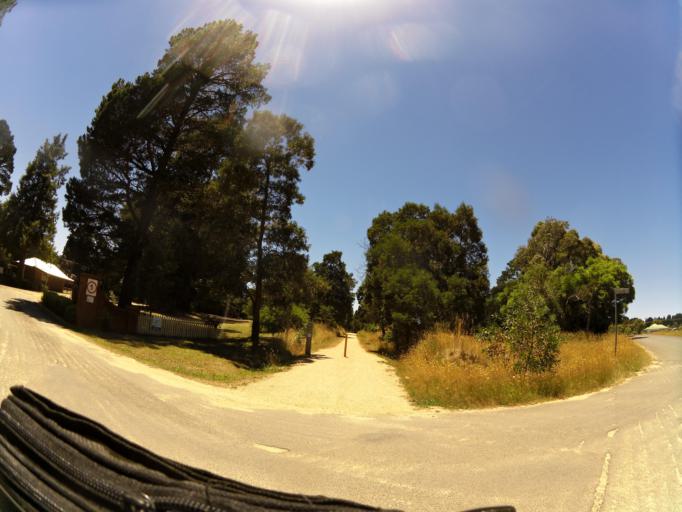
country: AU
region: Victoria
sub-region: Ballarat North
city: Delacombe
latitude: -37.6397
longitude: 143.6862
